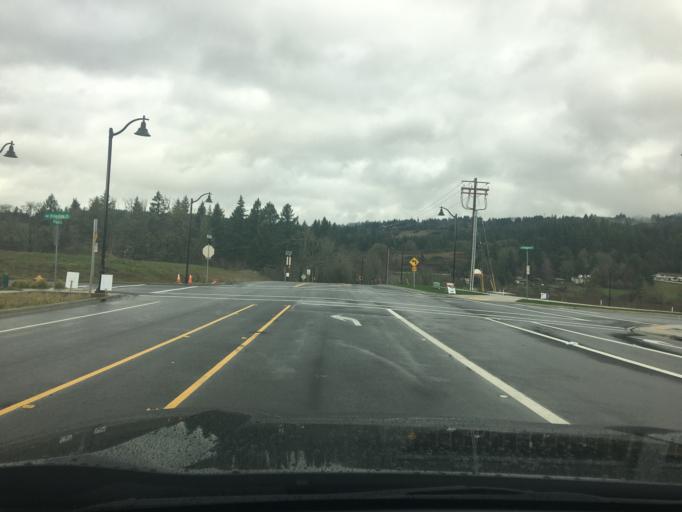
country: US
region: Oregon
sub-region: Washington County
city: Oak Hills
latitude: 45.5757
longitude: -122.8367
